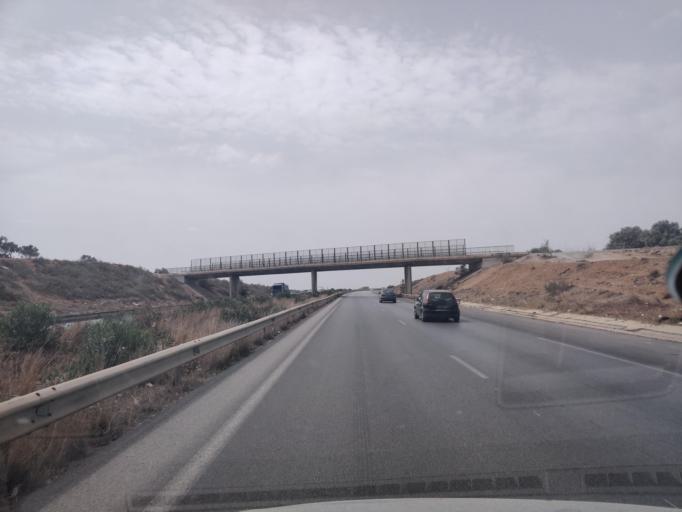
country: TN
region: Susah
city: Sidi Bou Ali
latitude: 35.9604
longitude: 10.4913
